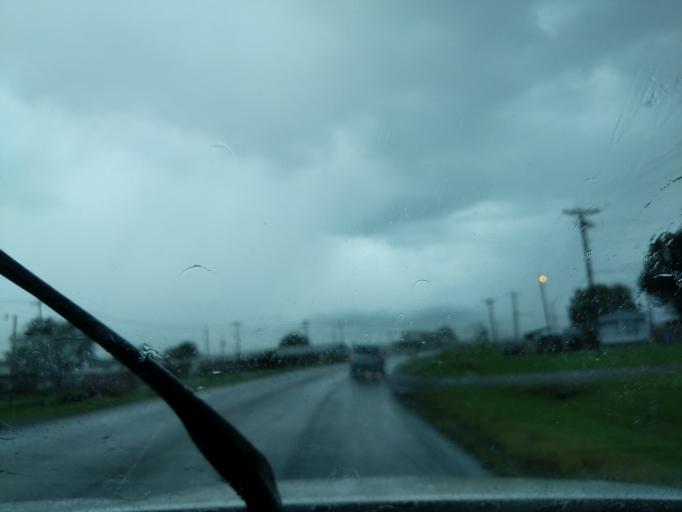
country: US
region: Missouri
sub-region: New Madrid County
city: New Madrid
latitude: 36.5967
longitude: -89.5346
